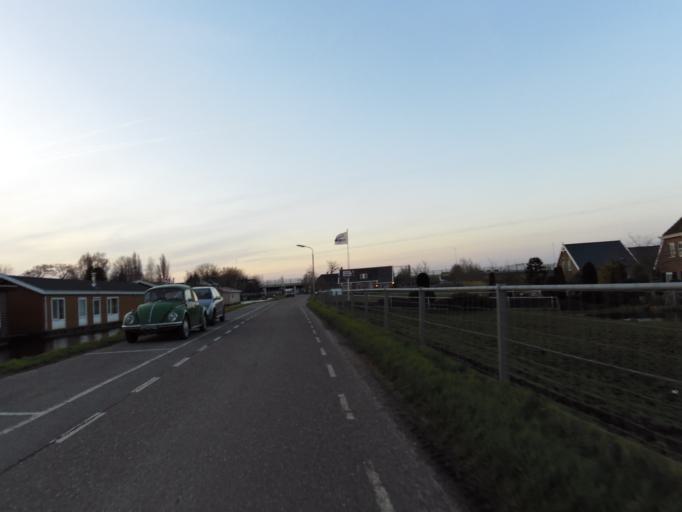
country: NL
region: South Holland
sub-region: Gemeente Kaag en Braassem
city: Oude Wetering
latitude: 52.1793
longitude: 4.5951
